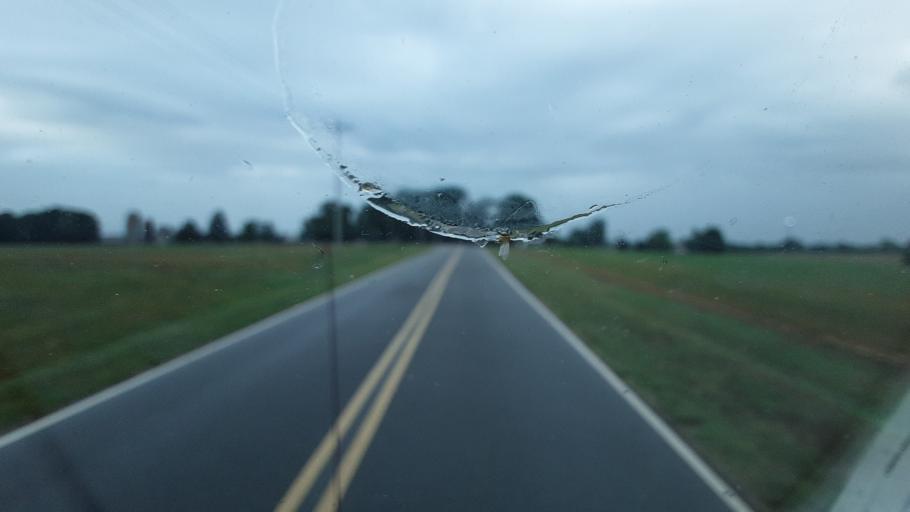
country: US
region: North Carolina
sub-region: Yadkin County
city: Jonesville
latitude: 36.0508
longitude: -80.8319
